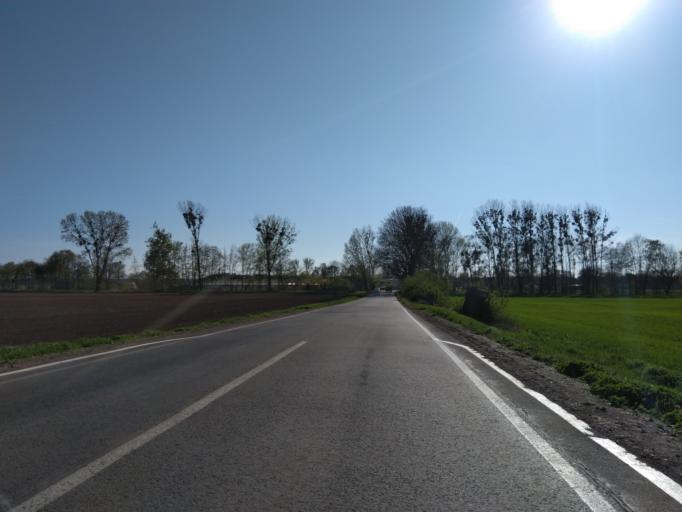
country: DE
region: Brandenburg
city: Bliesdorf
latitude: 52.6956
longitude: 14.1706
